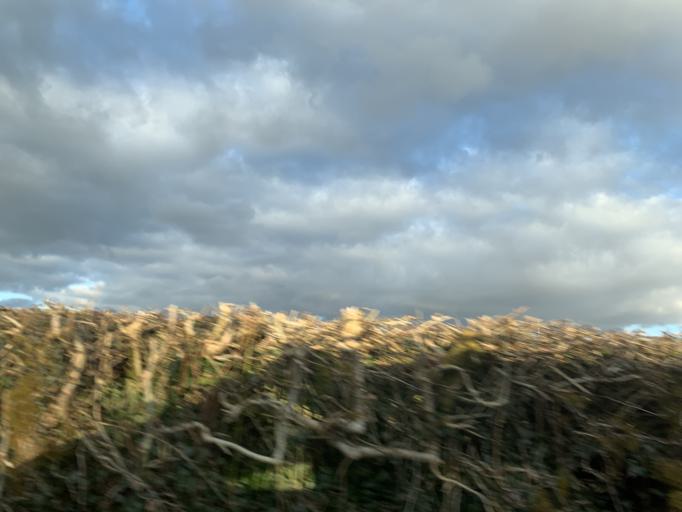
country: IE
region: Connaught
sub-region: Maigh Eo
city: Ballyhaunis
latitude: 53.8214
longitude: -8.6993
